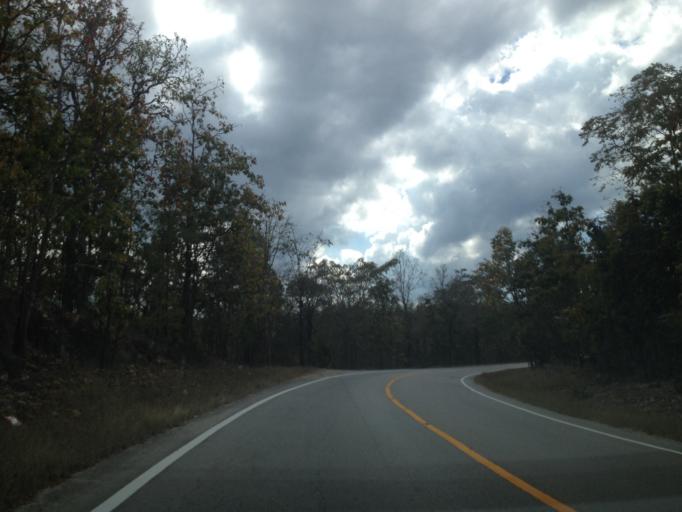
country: TH
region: Chiang Mai
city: Hot
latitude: 18.1691
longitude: 98.4438
